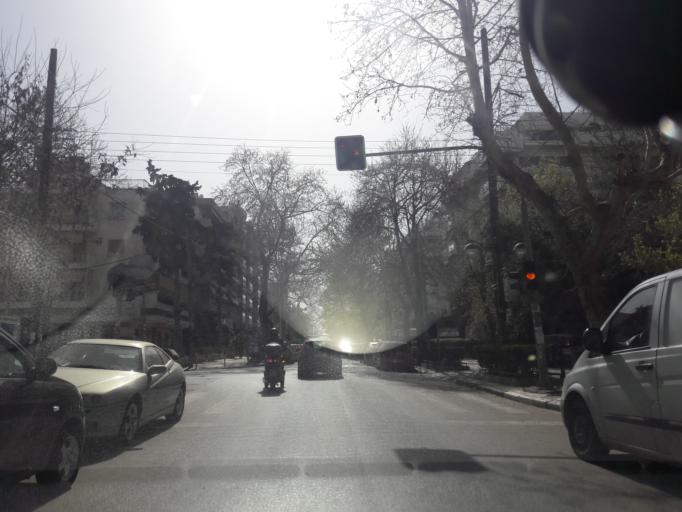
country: GR
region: Central Macedonia
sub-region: Nomos Thessalonikis
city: Kalamaria
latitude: 40.5921
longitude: 22.9490
